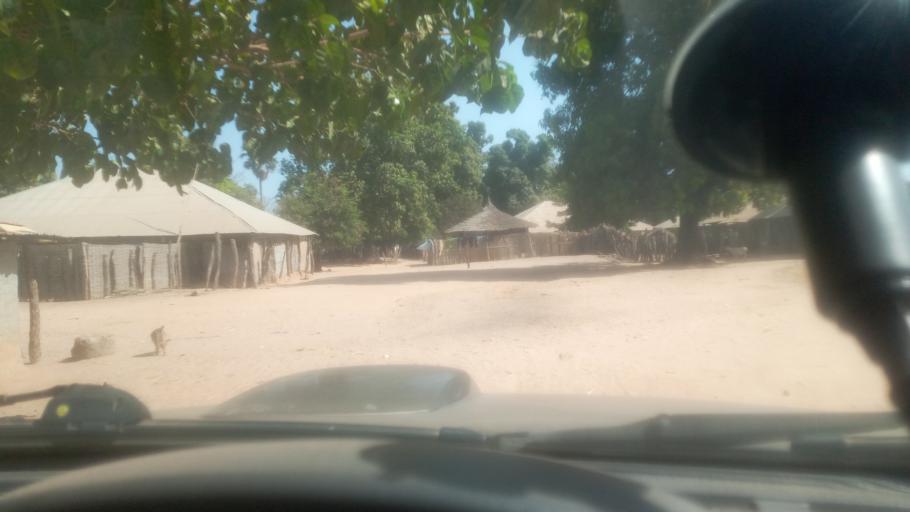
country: GW
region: Oio
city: Farim
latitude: 12.4604
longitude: -15.4071
